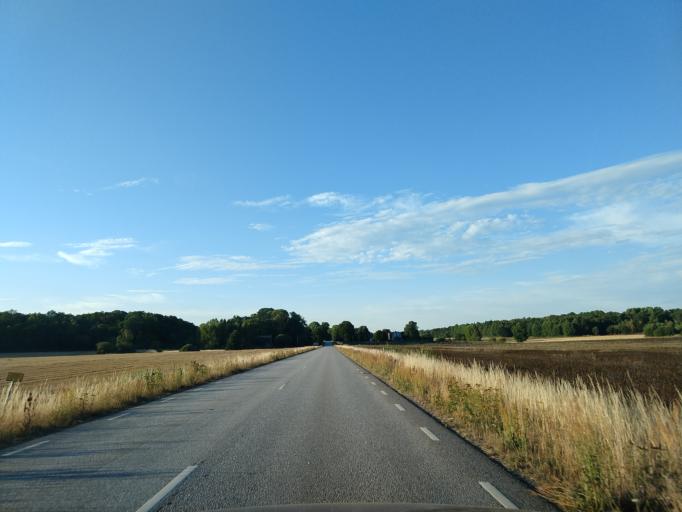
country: SE
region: Blekinge
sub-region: Ronneby Kommun
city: Brakne-Hoby
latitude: 56.2486
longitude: 15.1153
